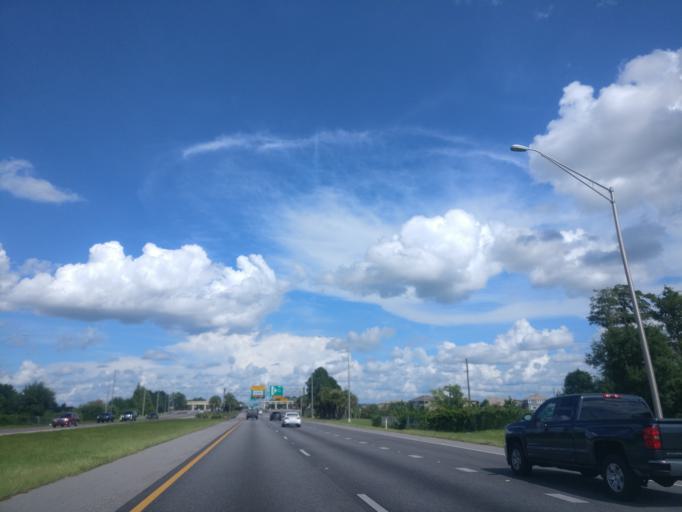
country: US
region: Florida
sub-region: Orange County
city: Meadow Woods
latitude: 28.3679
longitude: -81.3418
